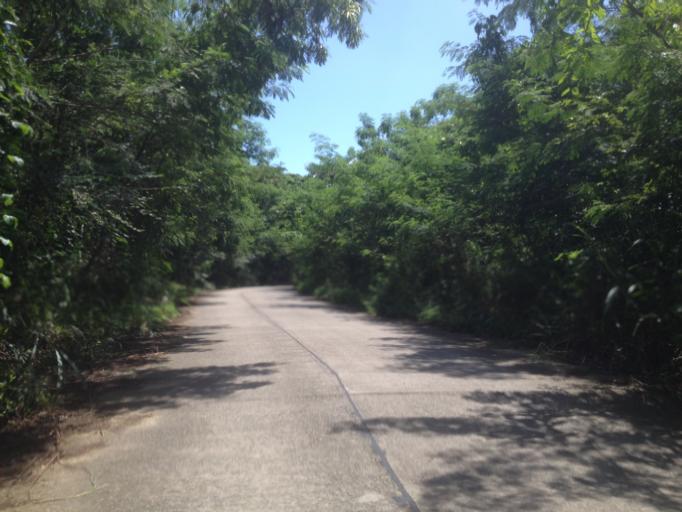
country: TH
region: Chiang Mai
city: Chiang Mai
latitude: 18.7670
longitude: 98.9377
